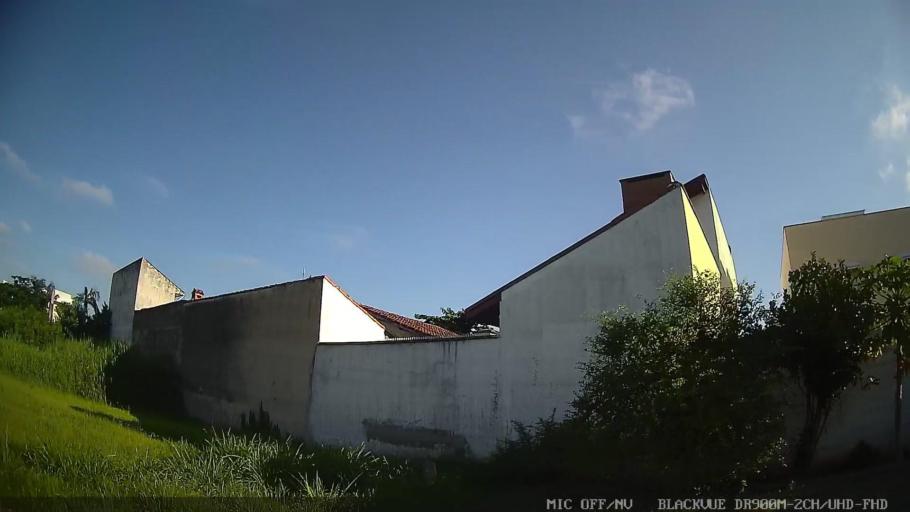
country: BR
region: Sao Paulo
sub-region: Peruibe
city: Peruibe
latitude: -24.2872
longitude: -46.9595
